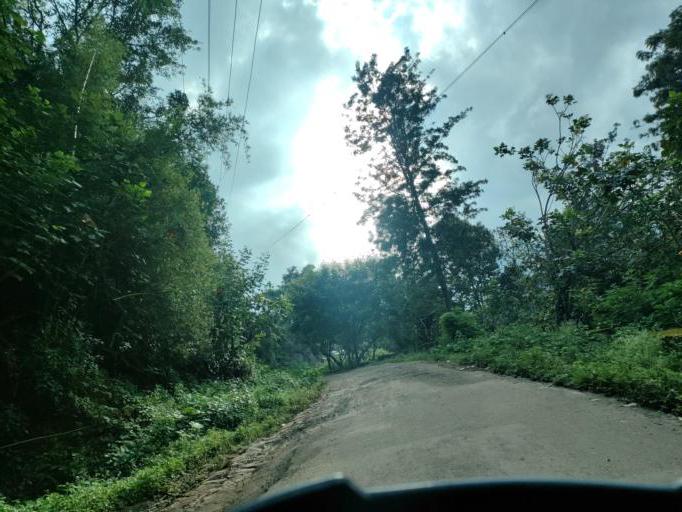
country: IN
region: Tamil Nadu
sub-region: Dindigul
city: Kodaikanal
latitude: 10.2843
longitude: 77.5324
